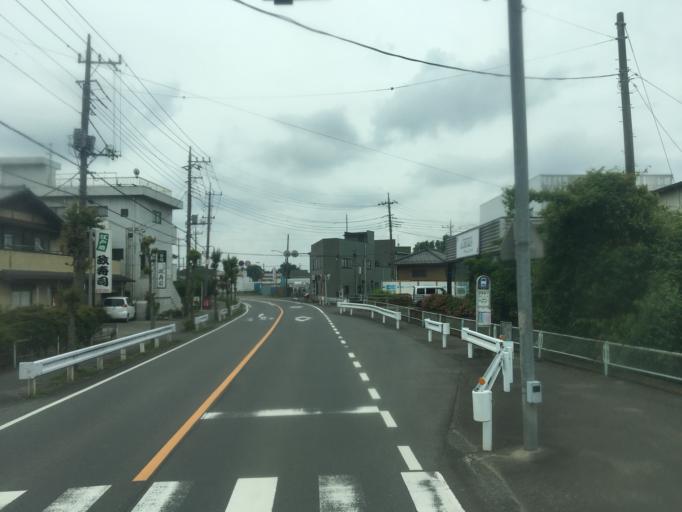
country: JP
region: Saitama
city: Kawagoe
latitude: 35.9718
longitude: 139.4624
